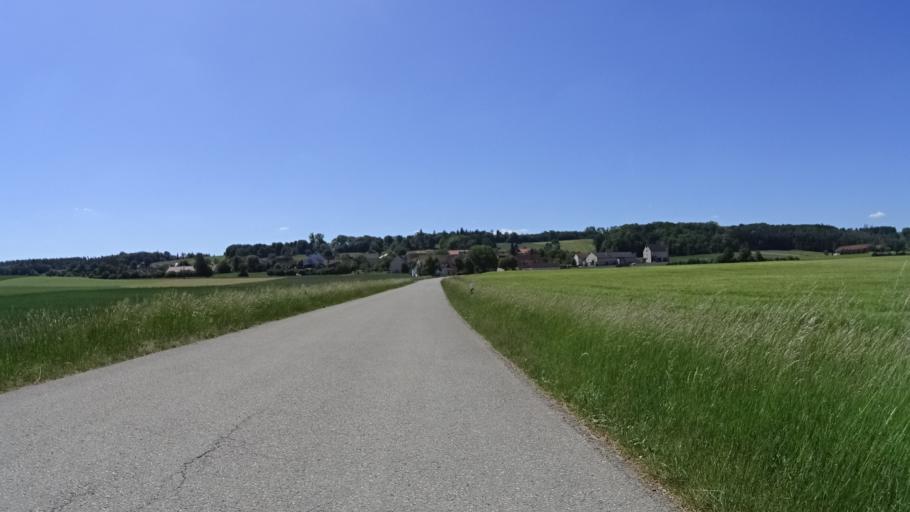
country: DE
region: Bavaria
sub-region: Regierungsbezirk Mittelfranken
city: Absberg
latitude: 49.1136
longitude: 10.8885
